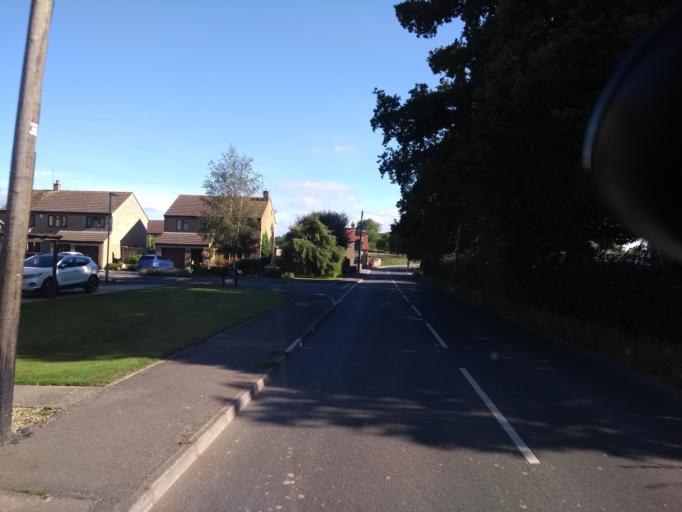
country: GB
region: England
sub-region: Somerset
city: Martock
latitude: 50.9802
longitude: -2.7661
